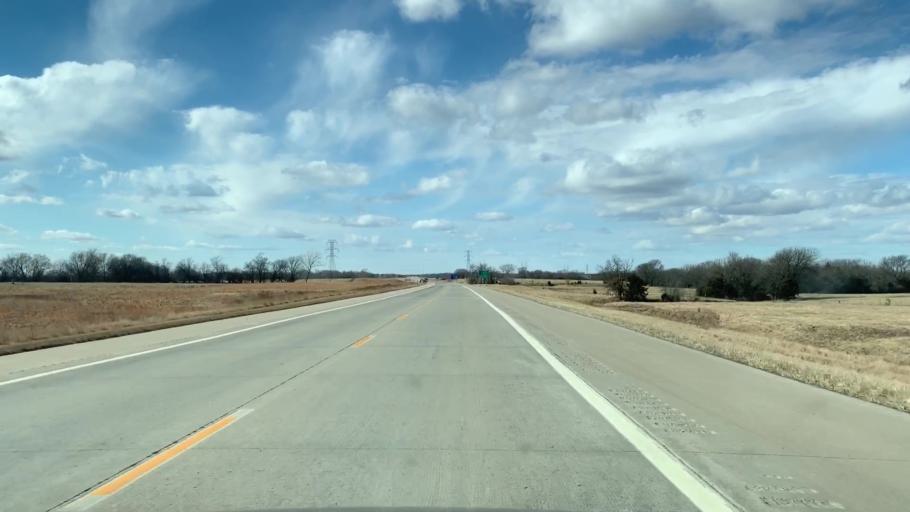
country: US
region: Kansas
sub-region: Labette County
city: Parsons
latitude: 37.3629
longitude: -95.2352
